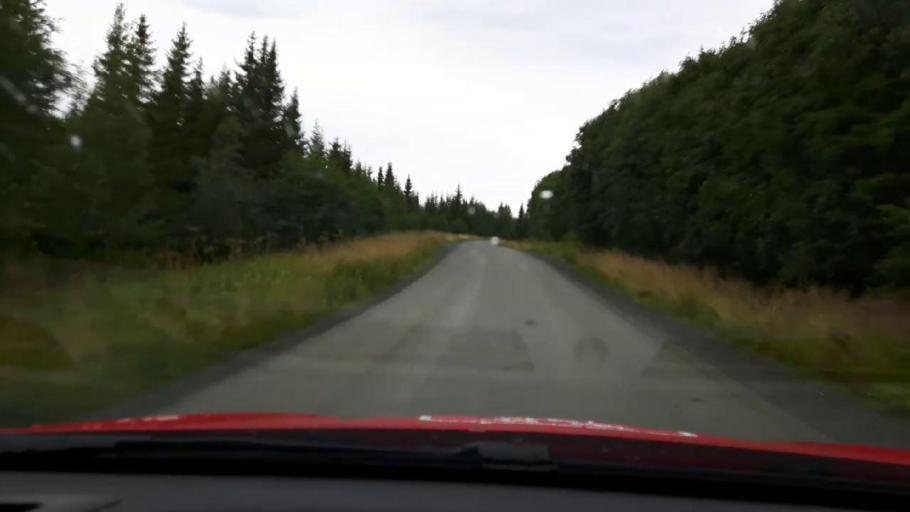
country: SE
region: Jaemtland
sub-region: Are Kommun
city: Are
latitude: 63.4556
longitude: 12.8159
